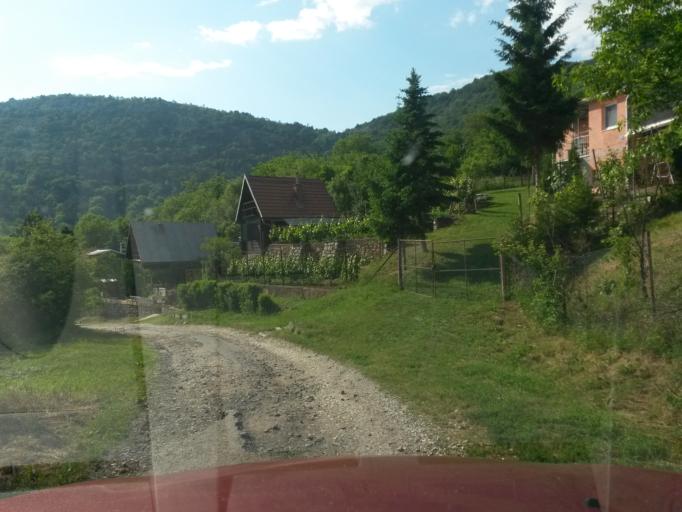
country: SK
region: Kosicky
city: Roznava
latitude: 48.5974
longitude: 20.6495
